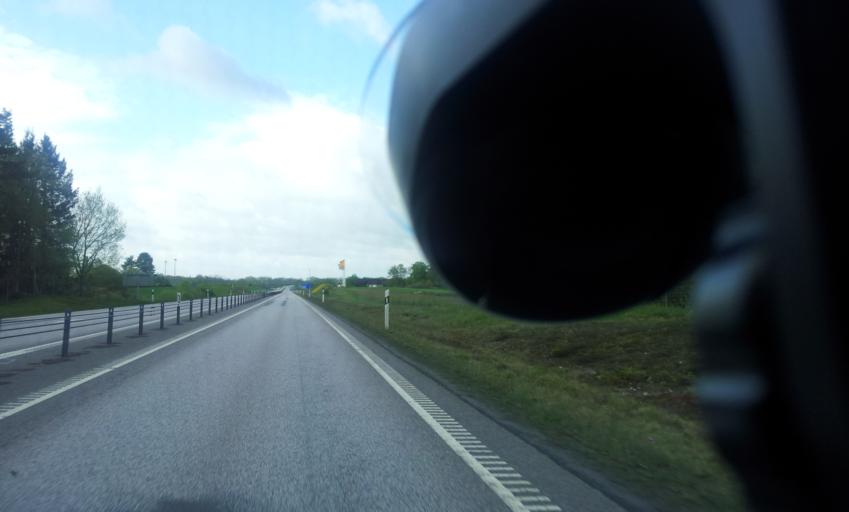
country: SE
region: Kalmar
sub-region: Torsas Kommun
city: Torsas
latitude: 56.4600
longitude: 16.0783
